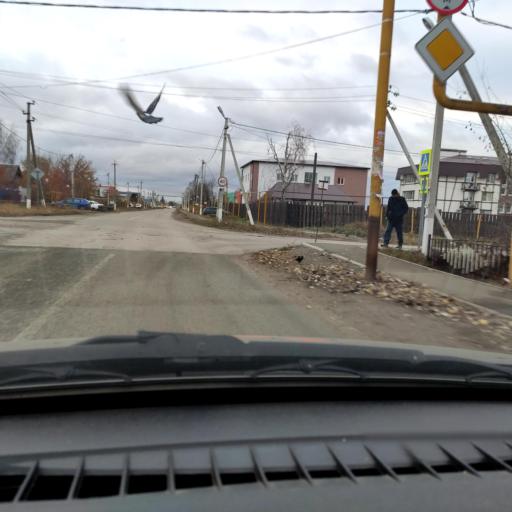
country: RU
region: Samara
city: Podstepki
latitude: 53.5165
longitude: 49.1168
